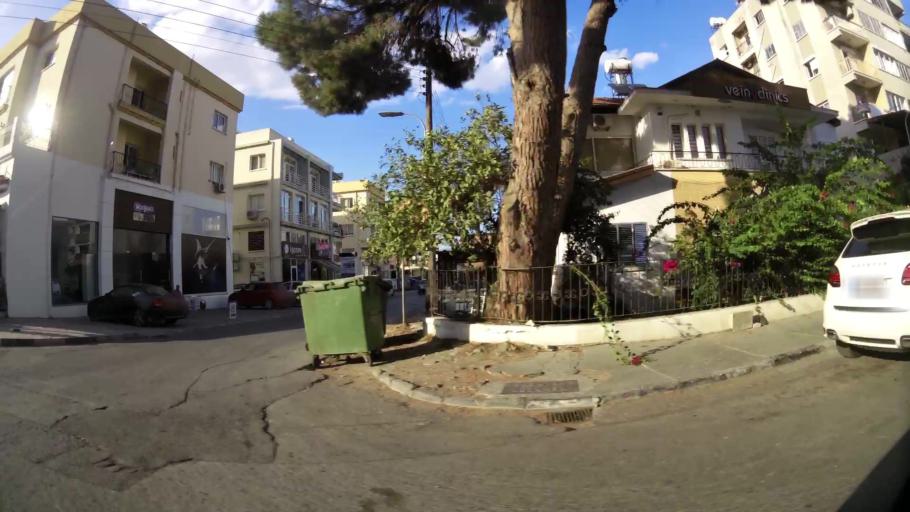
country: CY
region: Lefkosia
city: Nicosia
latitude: 35.1902
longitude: 33.3610
